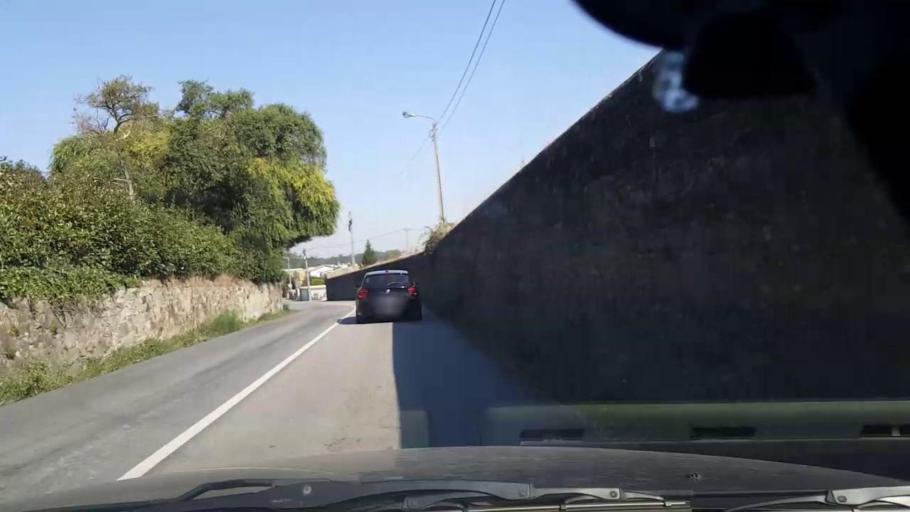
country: PT
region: Porto
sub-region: Vila do Conde
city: Arvore
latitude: 41.3316
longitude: -8.6807
